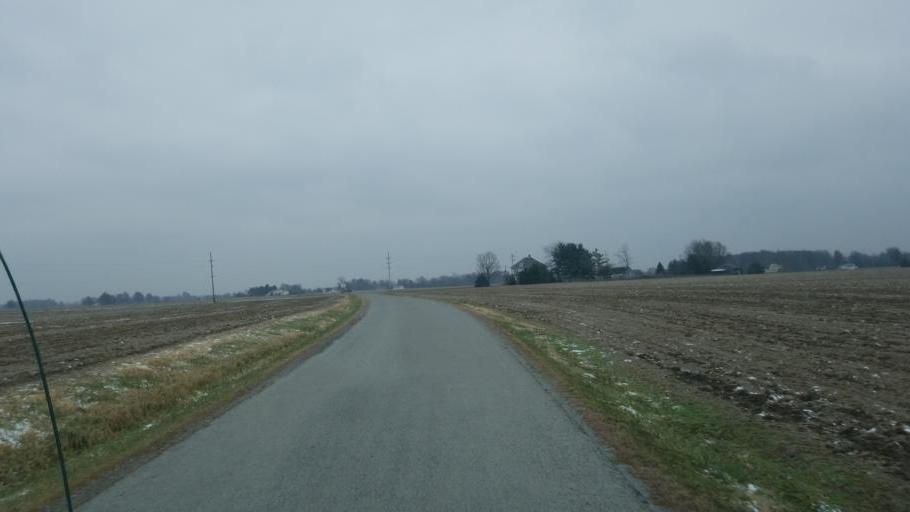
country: US
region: Ohio
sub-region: Crawford County
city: Crestline
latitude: 40.8470
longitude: -82.7324
